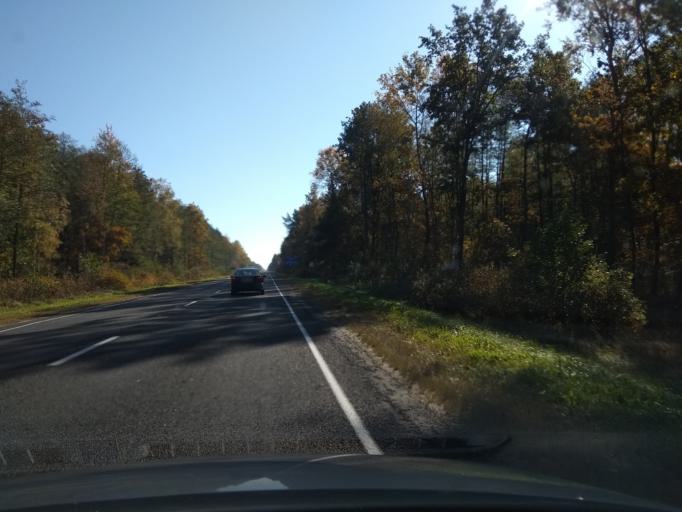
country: BY
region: Brest
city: Malaryta
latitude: 51.8954
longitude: 24.1333
